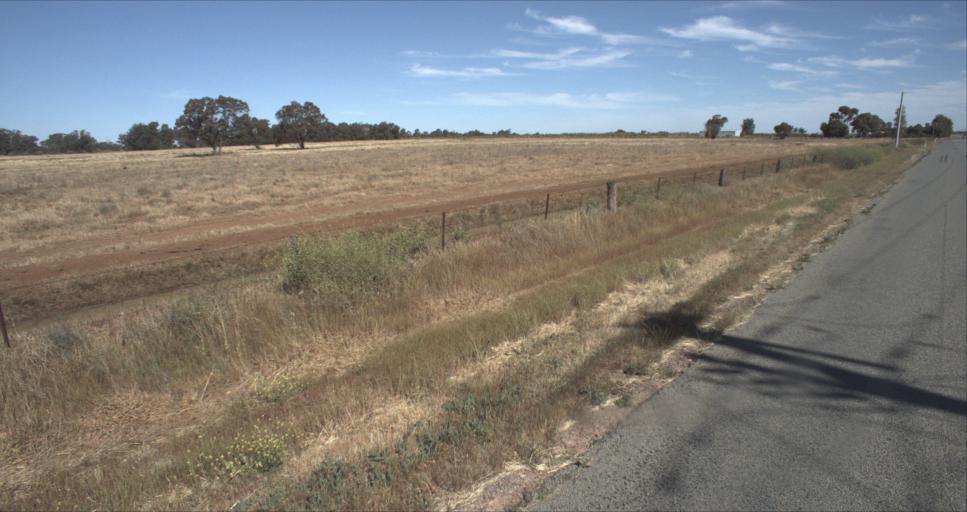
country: AU
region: New South Wales
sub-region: Leeton
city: Leeton
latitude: -34.5609
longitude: 146.3836
